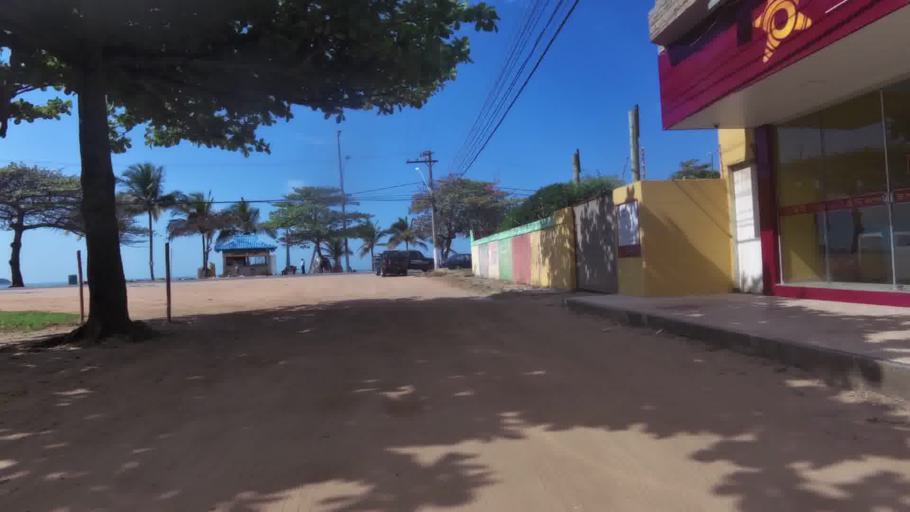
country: BR
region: Espirito Santo
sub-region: Piuma
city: Piuma
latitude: -20.8506
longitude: -40.7477
